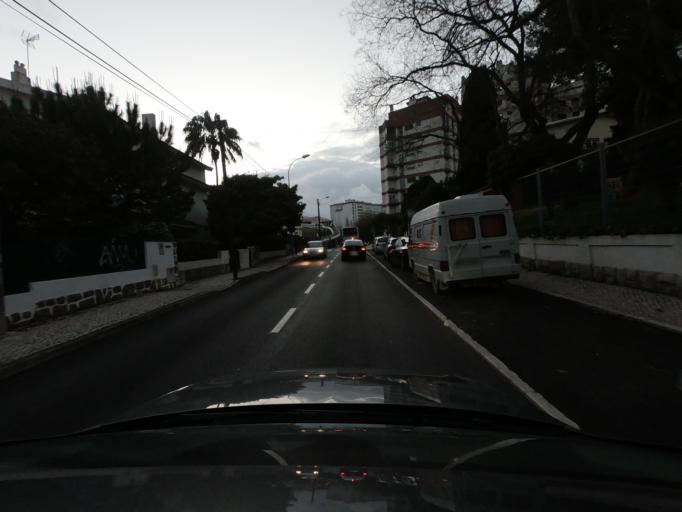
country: PT
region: Lisbon
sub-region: Oeiras
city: Paco de Arcos
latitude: 38.6993
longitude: -9.2918
